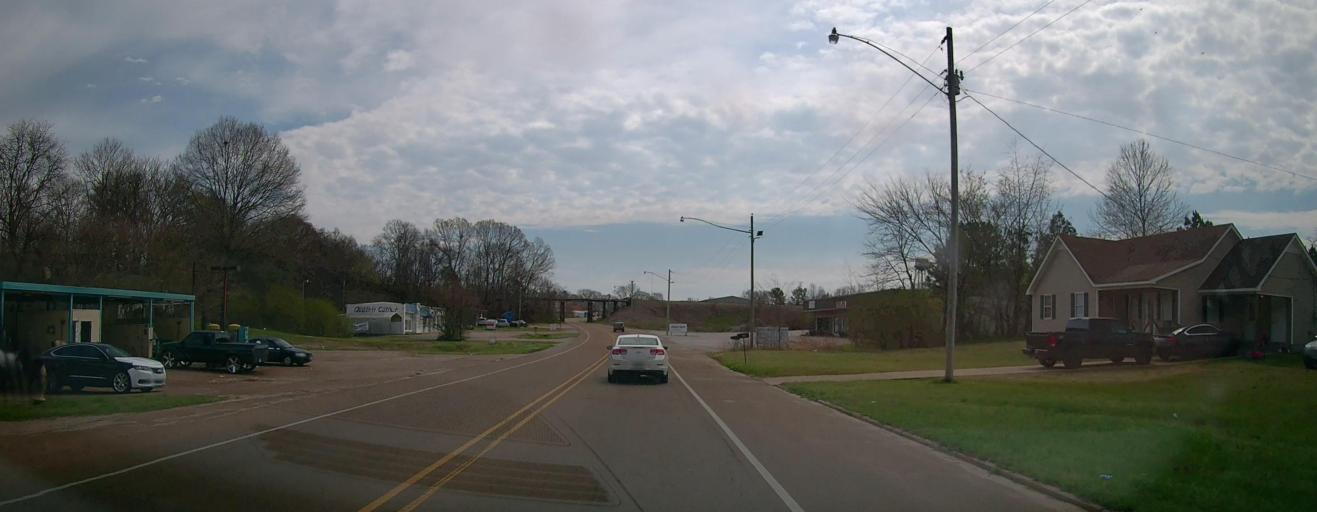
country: US
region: Mississippi
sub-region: Marshall County
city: Holly Springs
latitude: 34.7669
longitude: -89.4361
